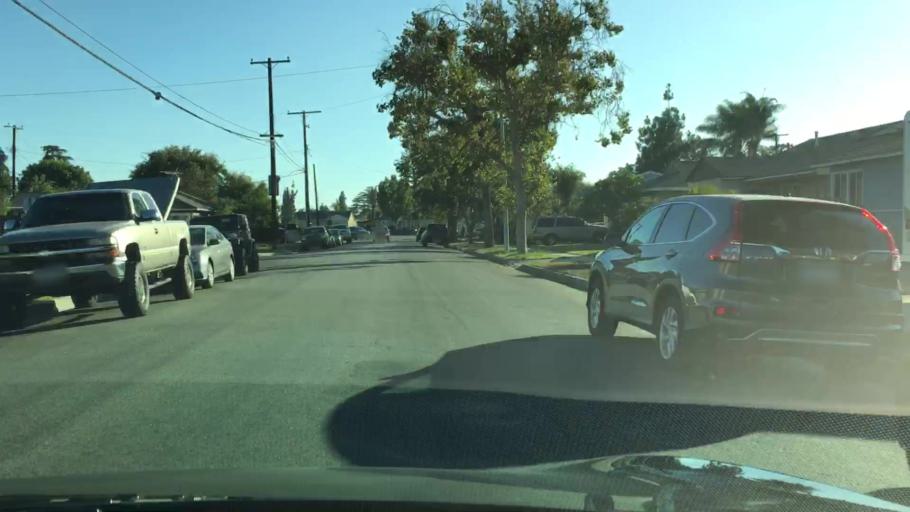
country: US
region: California
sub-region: Los Angeles County
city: Pico Rivera
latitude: 33.9793
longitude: -118.0873
